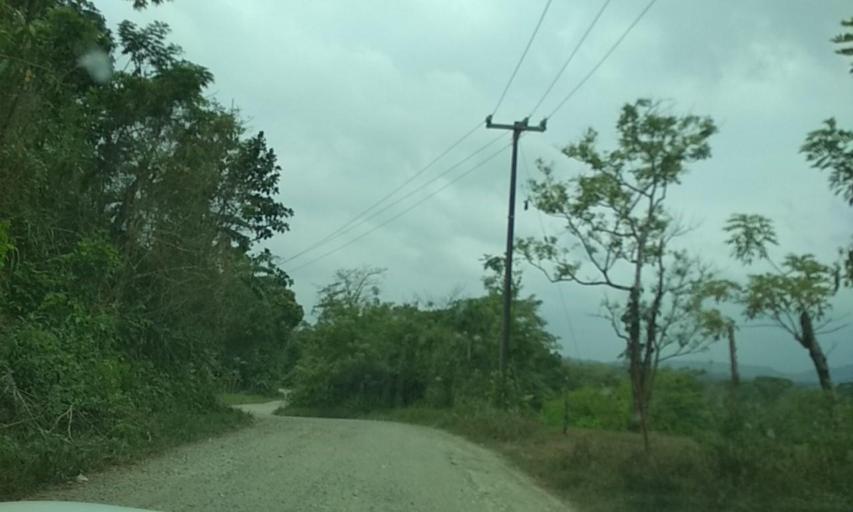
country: MX
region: Veracruz
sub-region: Uxpanapa
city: Poblado 10
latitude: 17.4979
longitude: -94.1408
